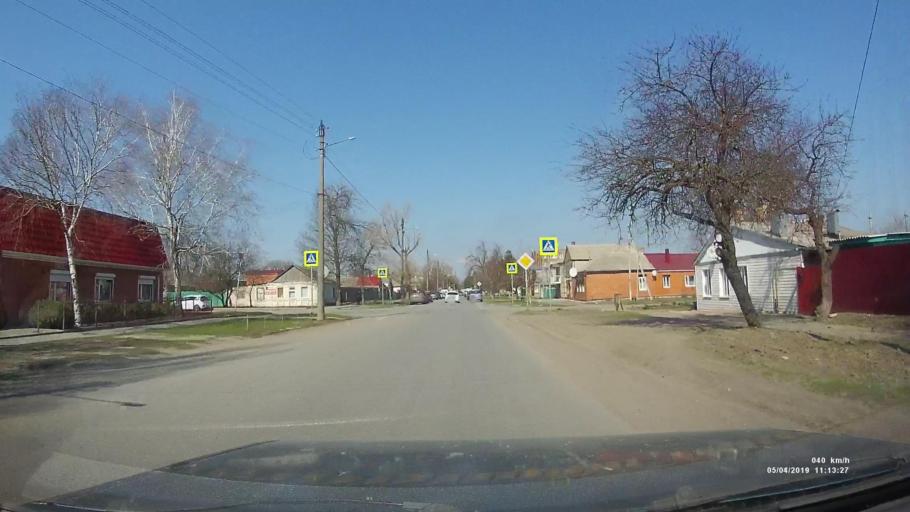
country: RU
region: Rostov
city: Azov
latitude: 47.1022
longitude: 39.4312
